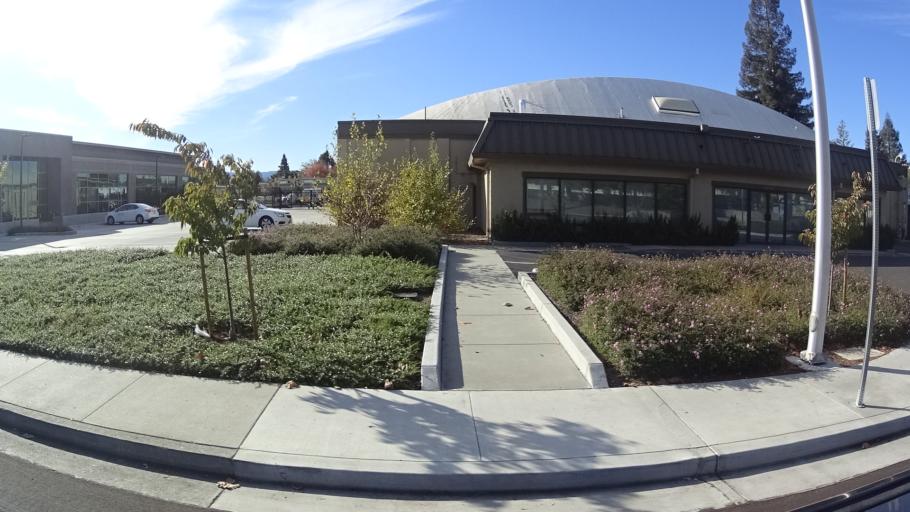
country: US
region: California
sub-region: Santa Clara County
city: Santa Clara
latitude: 37.3688
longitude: -121.9596
